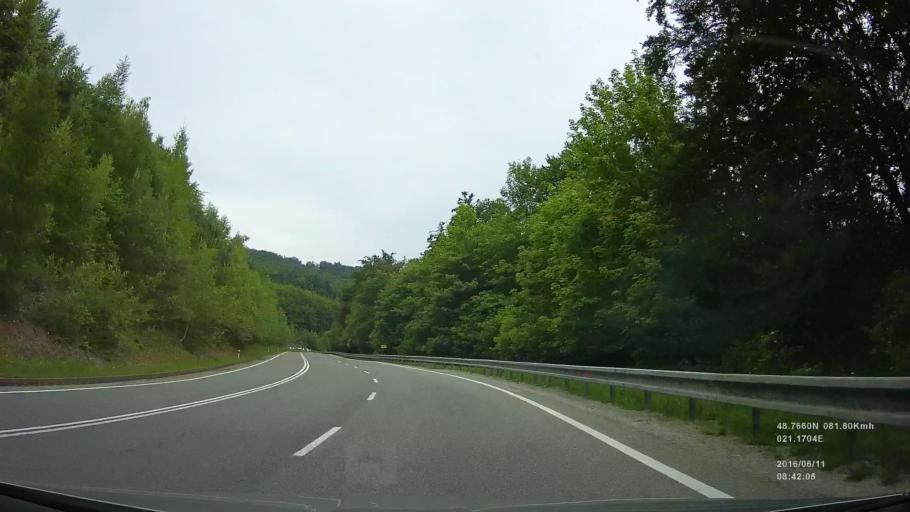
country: SK
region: Kosicky
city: Kosice
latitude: 48.7496
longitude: 21.2314
